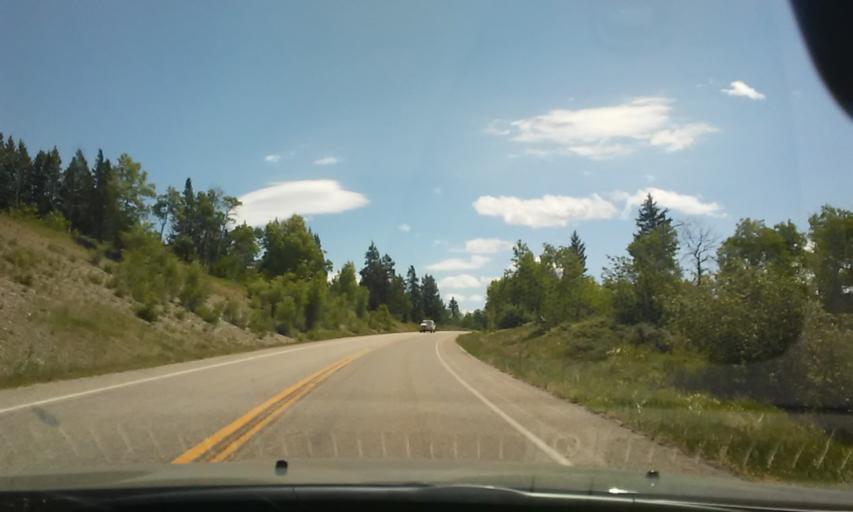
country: US
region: Wyoming
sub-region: Teton County
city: Jackson
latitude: 43.8392
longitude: -110.4888
